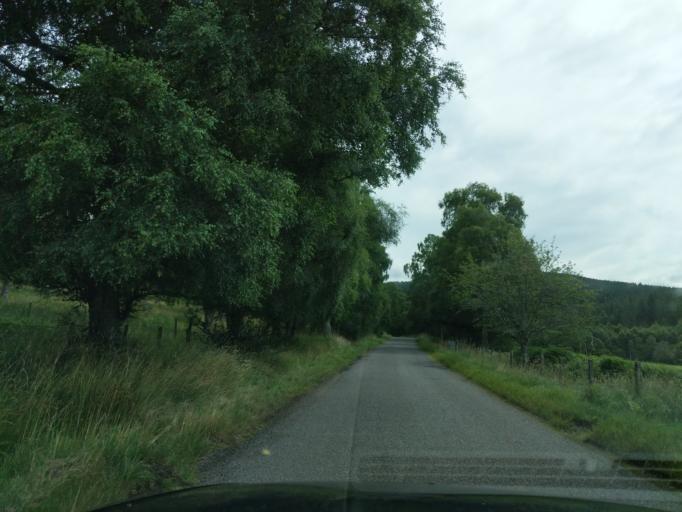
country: GB
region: Scotland
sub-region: Aberdeenshire
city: Aboyne
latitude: 57.0621
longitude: -2.8348
